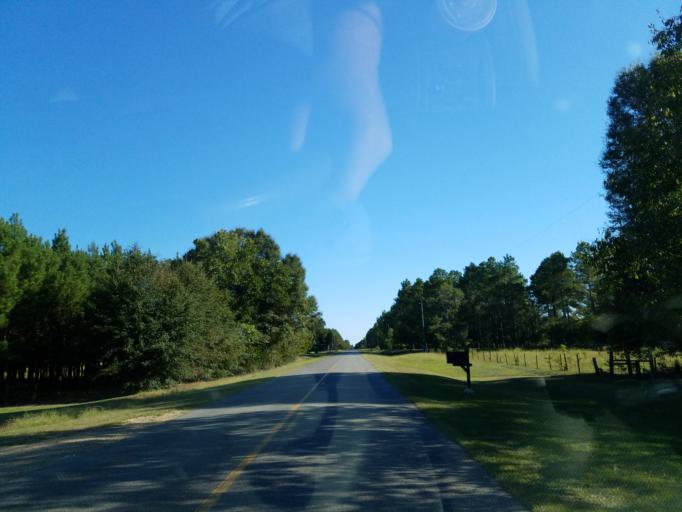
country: US
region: Georgia
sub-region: Dooly County
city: Vienna
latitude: 32.0522
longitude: -83.9494
